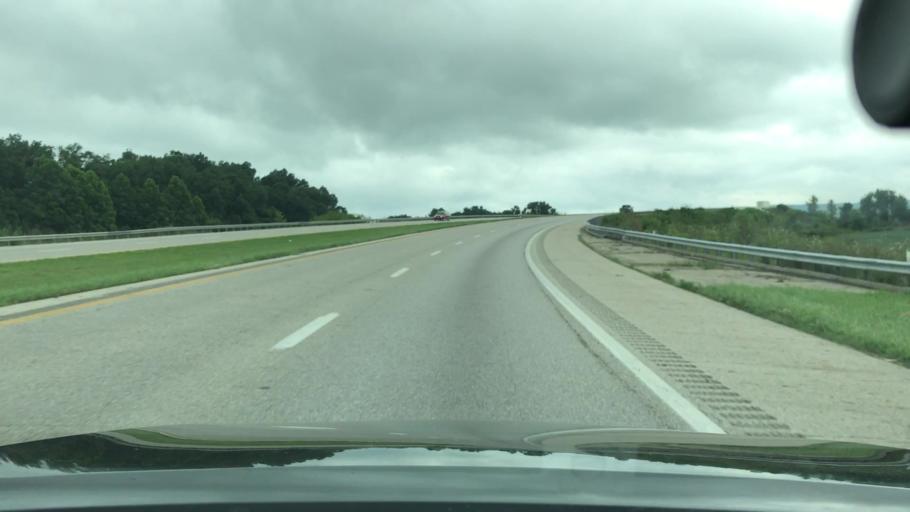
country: US
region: Ohio
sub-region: Ross County
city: Chillicothe
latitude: 39.2796
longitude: -82.8843
